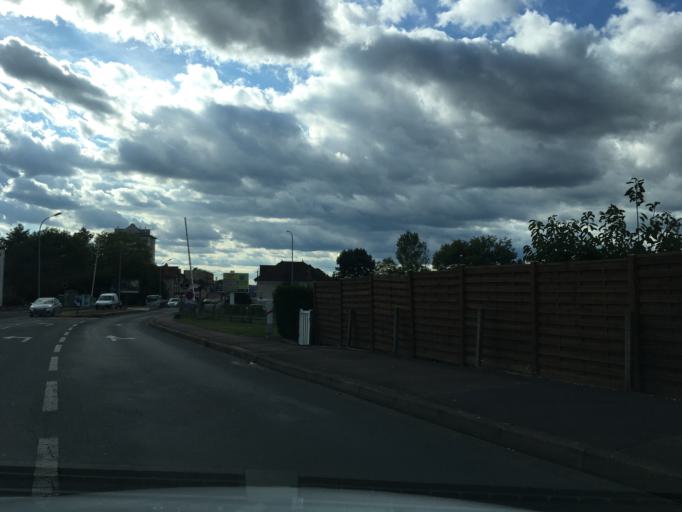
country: FR
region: Limousin
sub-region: Departement de la Correze
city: Malemort-sur-Correze
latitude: 45.1582
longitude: 1.5596
